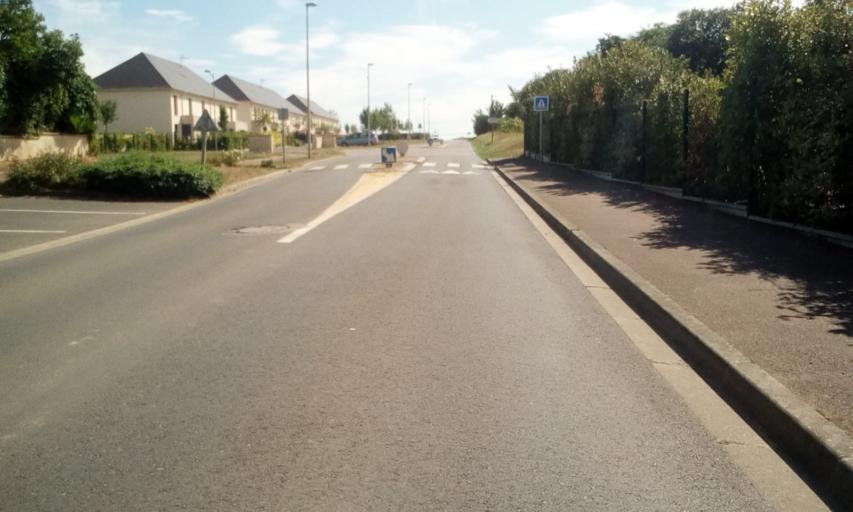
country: FR
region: Lower Normandy
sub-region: Departement du Calvados
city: Eterville
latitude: 49.1262
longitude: -0.4241
